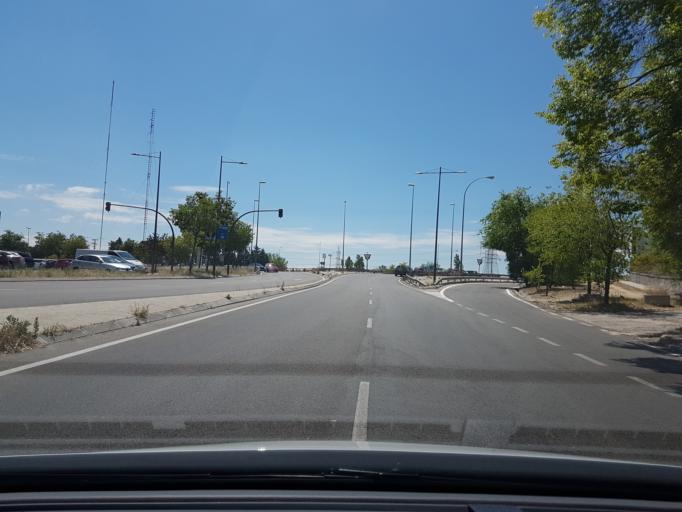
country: ES
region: Madrid
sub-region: Provincia de Madrid
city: Pozuelo de Alarcon
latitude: 40.4301
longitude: -3.8114
